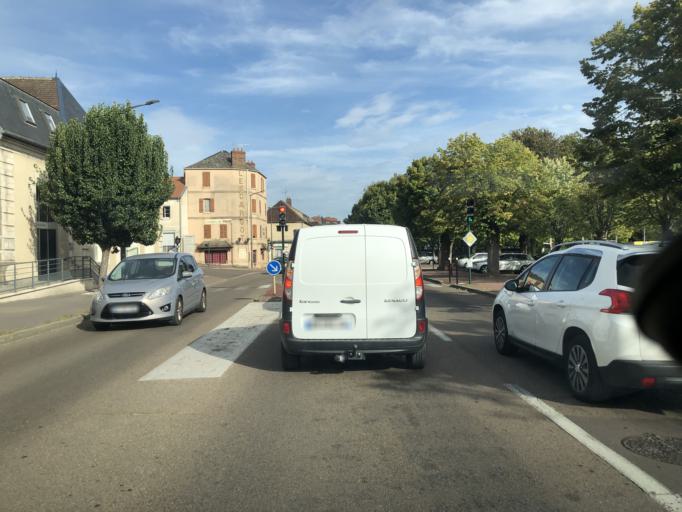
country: FR
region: Bourgogne
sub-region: Departement de l'Yonne
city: Joigny
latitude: 47.9807
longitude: 3.4002
